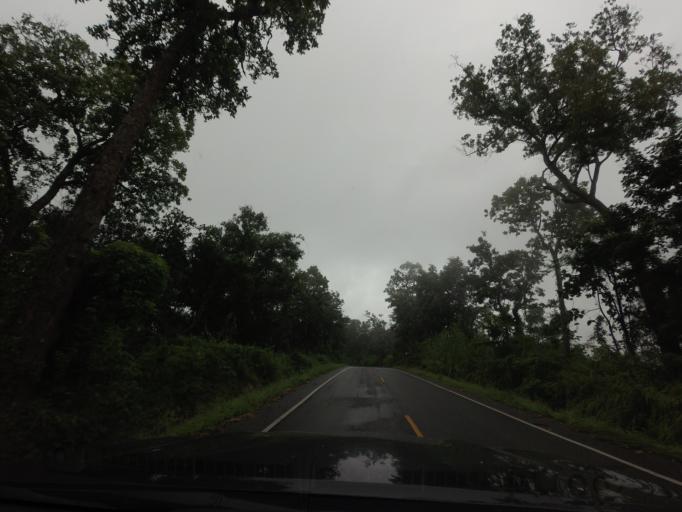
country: TH
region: Nong Khai
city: Sangkhom
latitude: 18.0386
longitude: 102.3248
